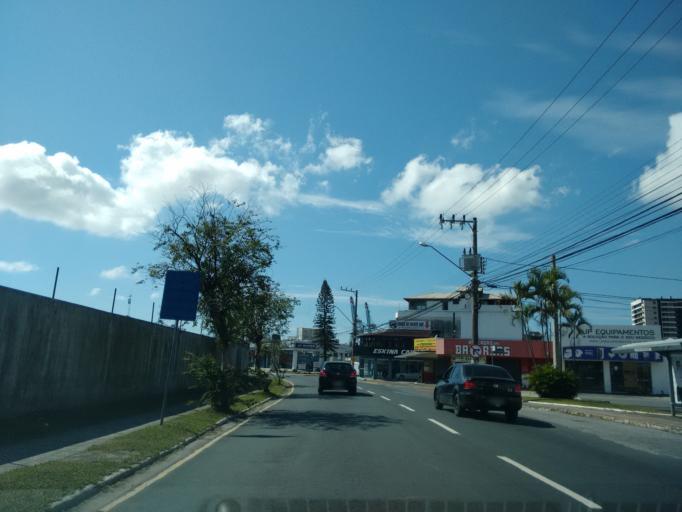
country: BR
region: Santa Catarina
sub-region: Itajai
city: Itajai
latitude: -26.9027
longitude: -48.6691
